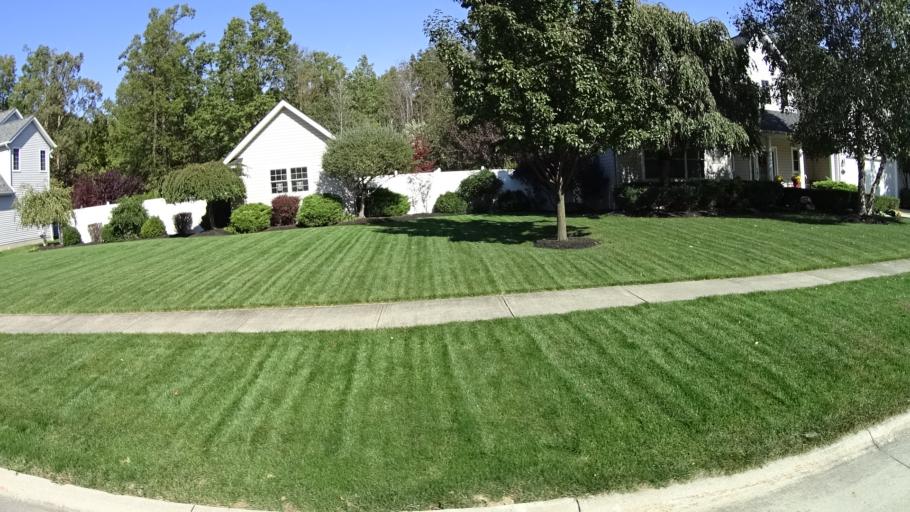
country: US
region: Ohio
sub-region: Lorain County
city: Vermilion-on-the-Lake
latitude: 41.4214
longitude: -82.3224
